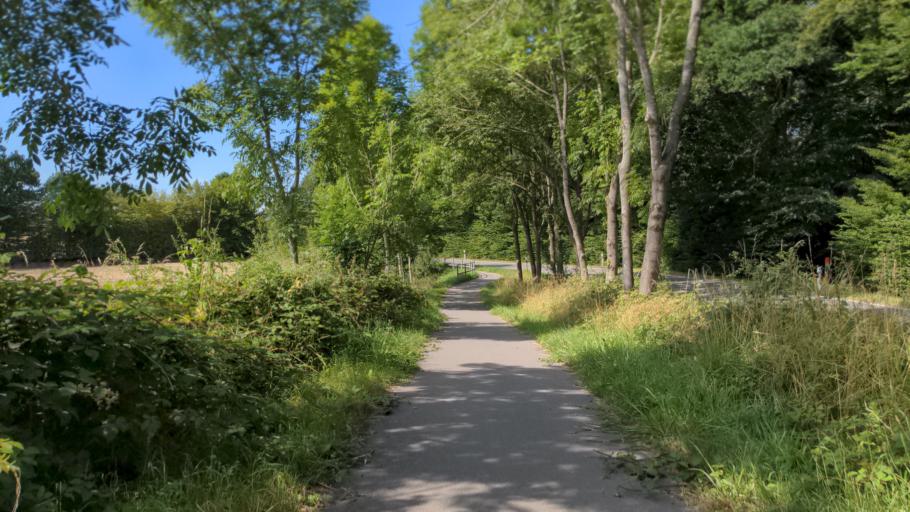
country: DE
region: Schleswig-Holstein
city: Grebin
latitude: 54.1924
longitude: 10.5188
